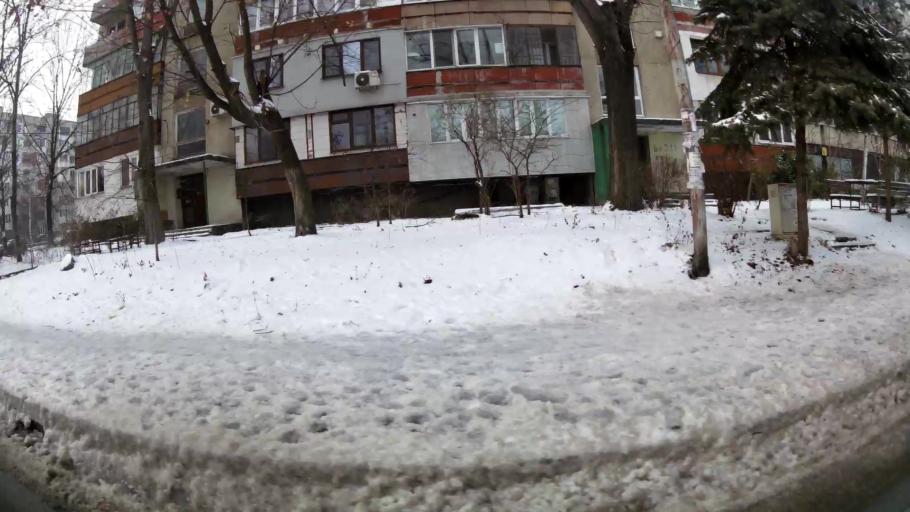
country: BG
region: Sofia-Capital
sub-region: Stolichna Obshtina
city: Sofia
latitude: 42.7151
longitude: 23.3063
